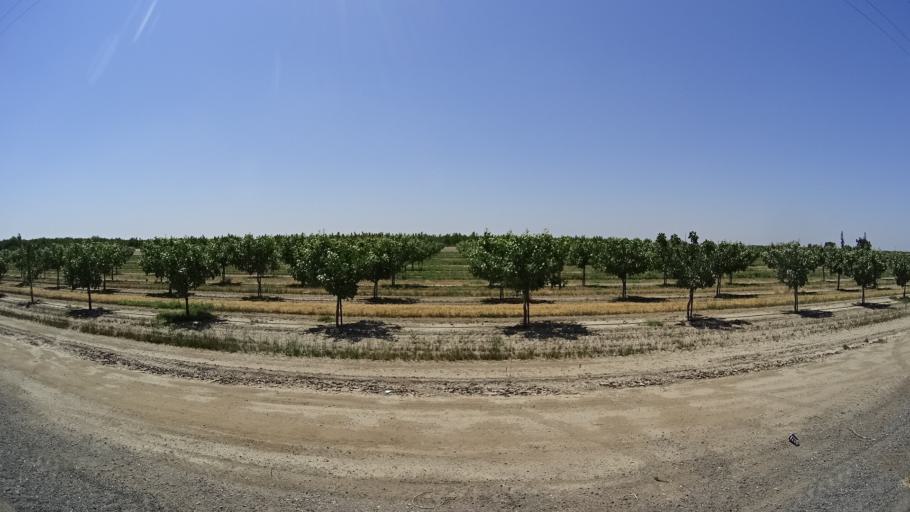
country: US
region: California
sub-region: Kings County
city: Armona
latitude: 36.3571
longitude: -119.7038
